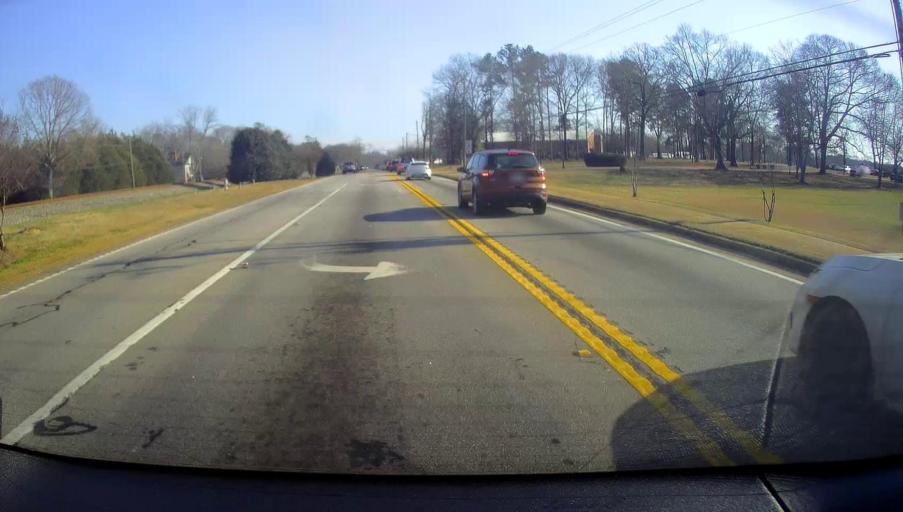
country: US
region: Georgia
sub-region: Henry County
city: Locust Grove
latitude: 33.3530
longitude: -84.1132
